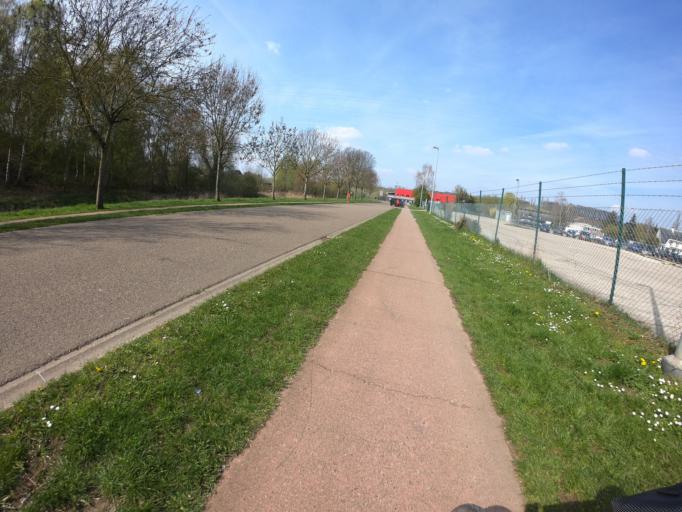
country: BE
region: Flanders
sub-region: Provincie Vlaams-Brabant
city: Diest
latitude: 50.9874
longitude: 5.0390
